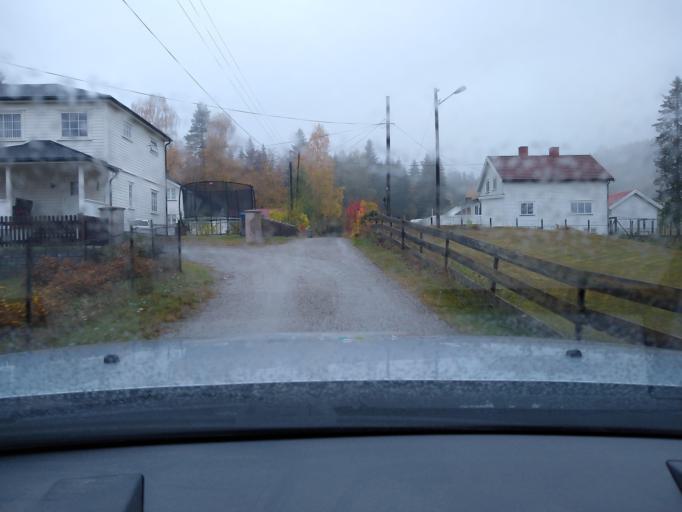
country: NO
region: Oppland
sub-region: Ringebu
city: Ringebu
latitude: 61.5352
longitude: 10.1455
